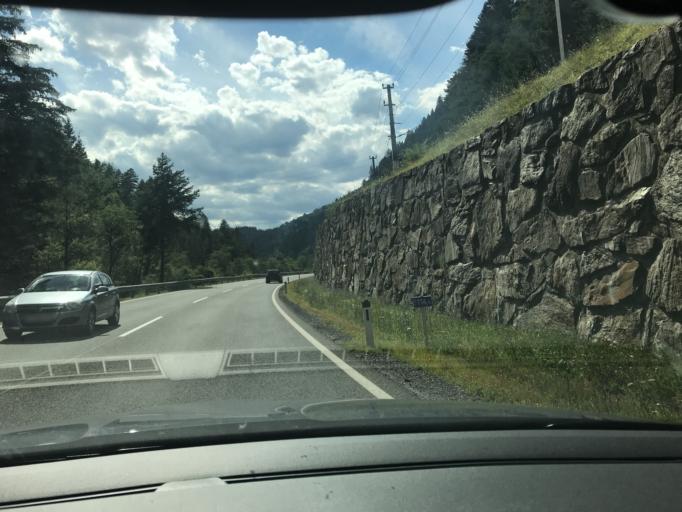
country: AT
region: Tyrol
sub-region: Politischer Bezirk Lienz
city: Leisach
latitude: 46.7918
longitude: 12.7170
